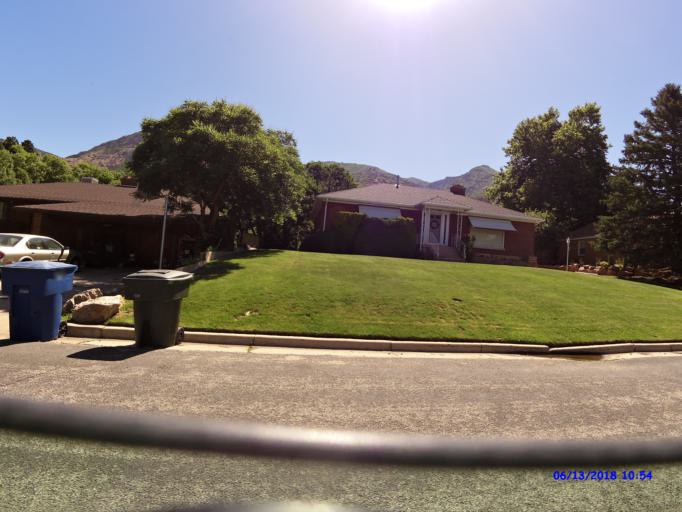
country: US
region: Utah
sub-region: Weber County
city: South Ogden
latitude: 41.2020
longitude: -111.9392
